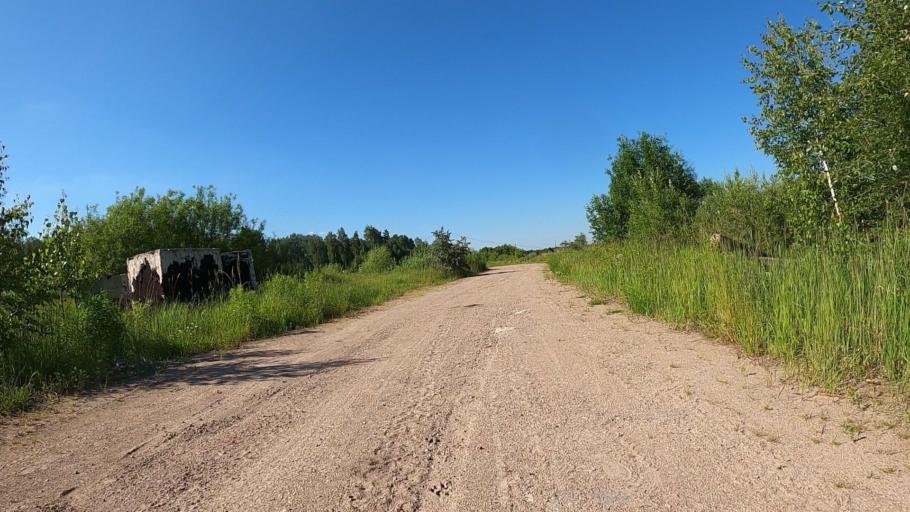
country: LV
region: Stopini
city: Ulbroka
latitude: 56.8781
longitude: 24.2771
